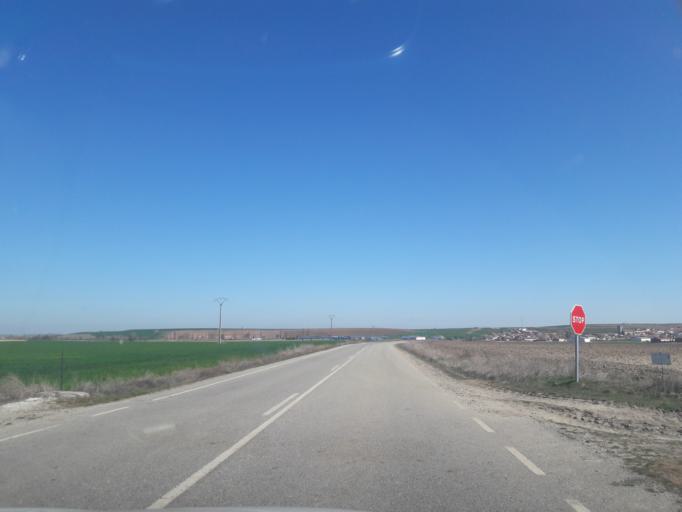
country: ES
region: Castille and Leon
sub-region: Provincia de Salamanca
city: Mancera de Abajo
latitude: 40.8296
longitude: -5.2072
